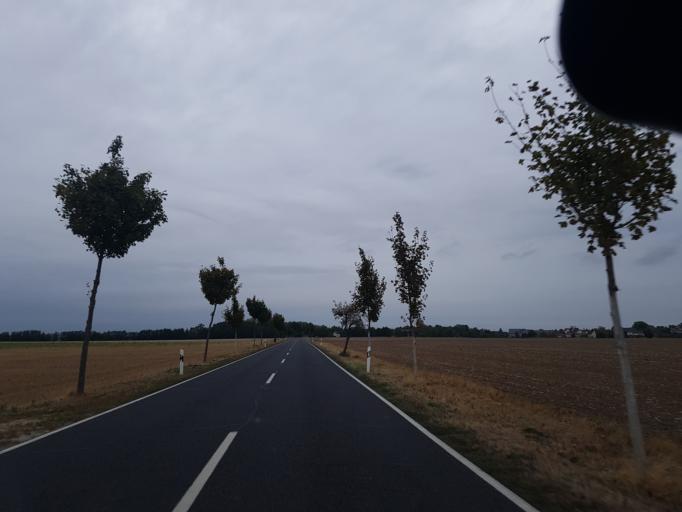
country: DE
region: Saxony-Anhalt
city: Prettin
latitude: 51.6932
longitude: 12.8926
